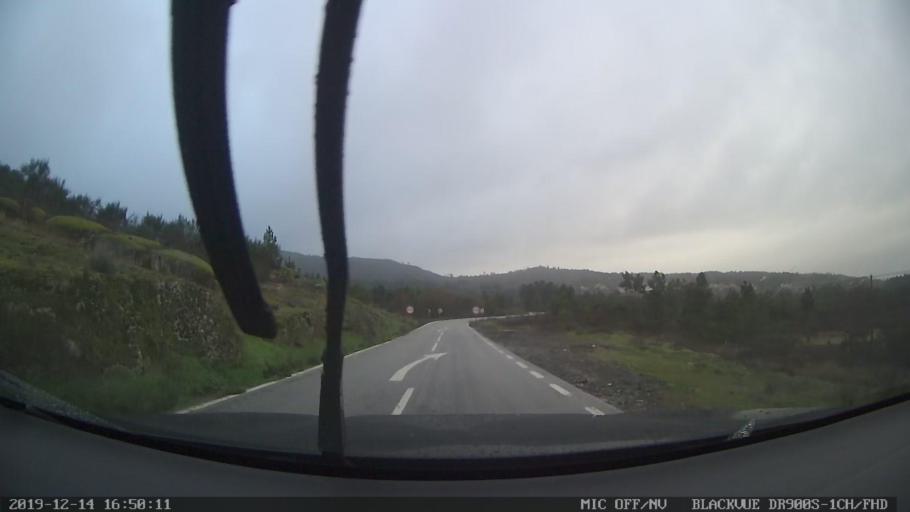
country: PT
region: Vila Real
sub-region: Murca
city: Murca
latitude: 41.4145
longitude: -7.5029
